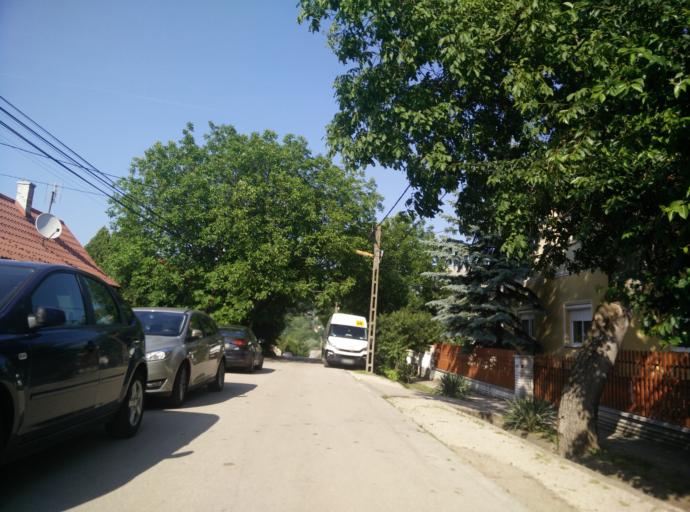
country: HU
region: Pest
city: Biatorbagy
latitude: 47.4807
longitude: 18.8231
